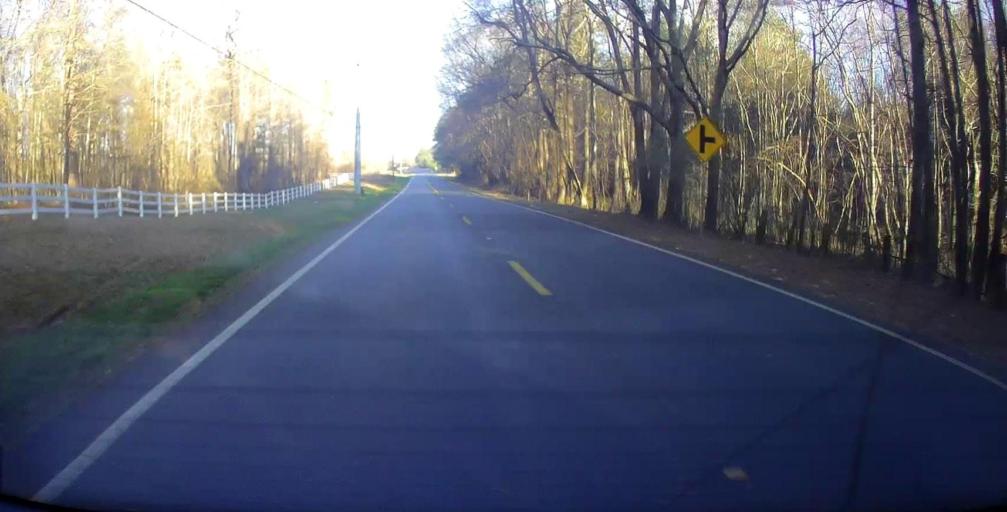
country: US
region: Georgia
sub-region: Harris County
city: Pine Mountain
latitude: 32.9162
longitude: -84.7820
